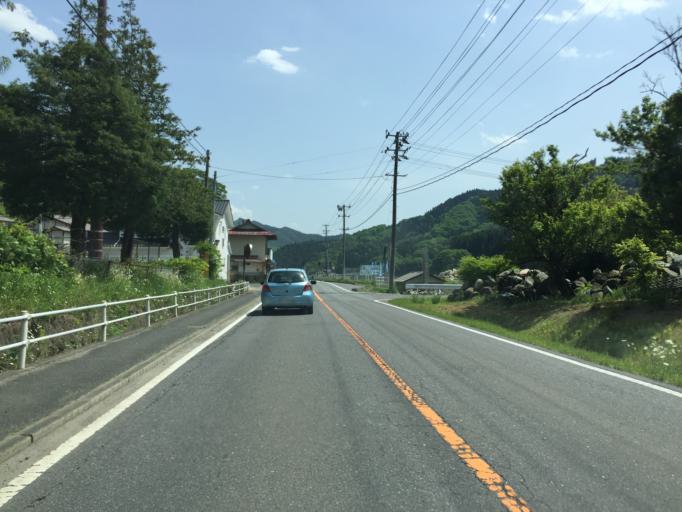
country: JP
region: Fukushima
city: Ishikawa
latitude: 37.0923
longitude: 140.5146
